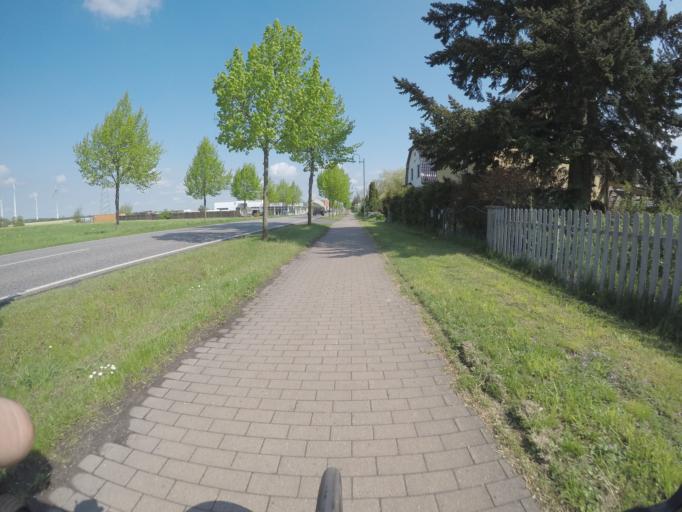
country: DE
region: Brandenburg
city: Wandlitz
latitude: 52.7816
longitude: 13.4796
